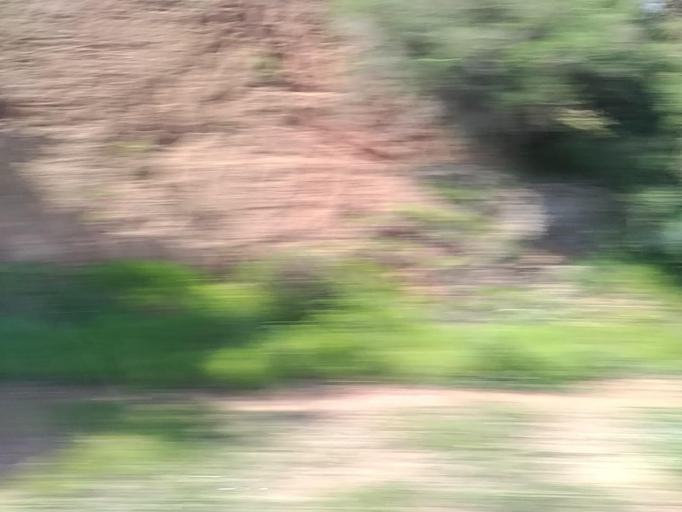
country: CL
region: Valparaiso
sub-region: Provincia de Valparaiso
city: Vina del Mar
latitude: -33.0505
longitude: -71.5307
